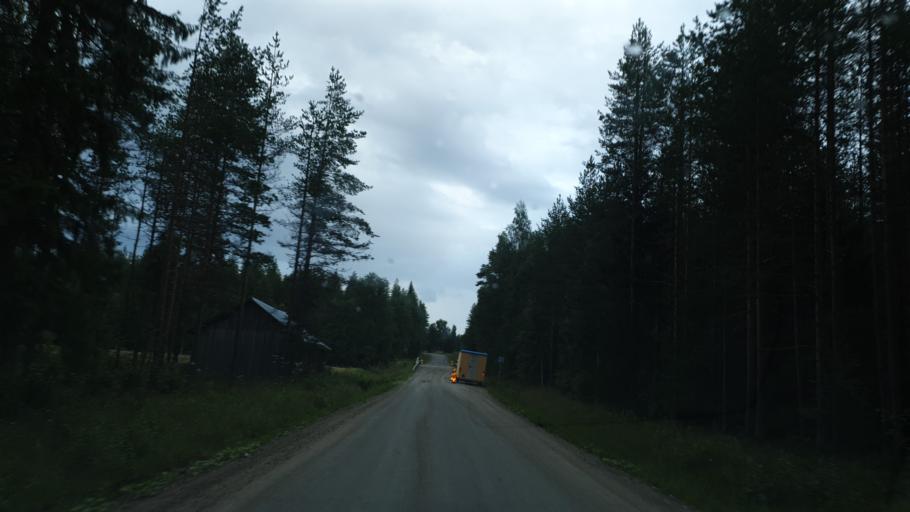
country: FI
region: Kainuu
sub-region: Kehys-Kainuu
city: Kuhmo
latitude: 64.2091
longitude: 29.3705
